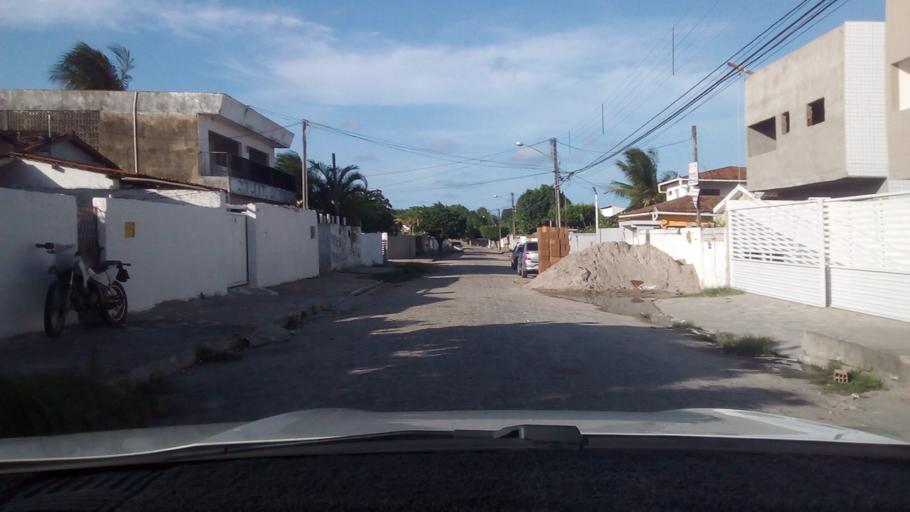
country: BR
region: Paraiba
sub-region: Joao Pessoa
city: Joao Pessoa
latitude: -7.1672
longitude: -34.8554
